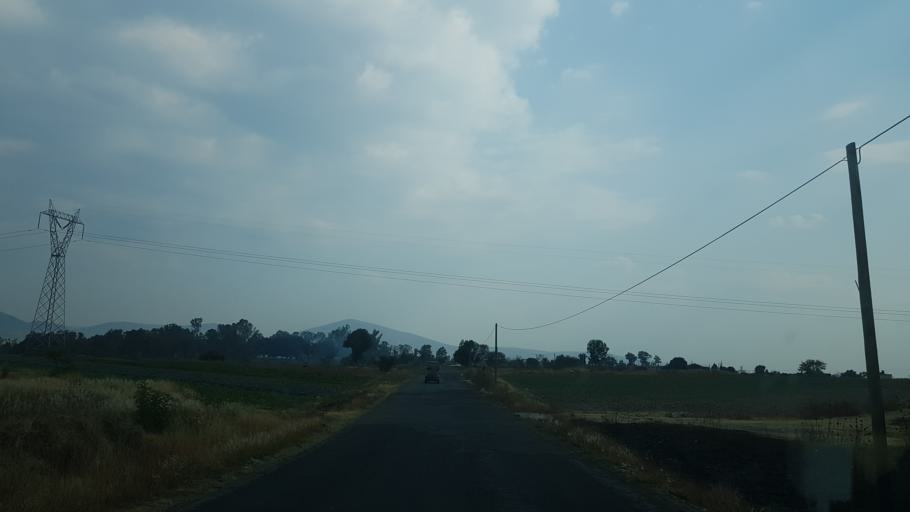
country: MX
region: Puebla
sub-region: Santa Isabel Cholula
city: Santa Ana Acozautla
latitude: 18.9539
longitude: -98.3944
